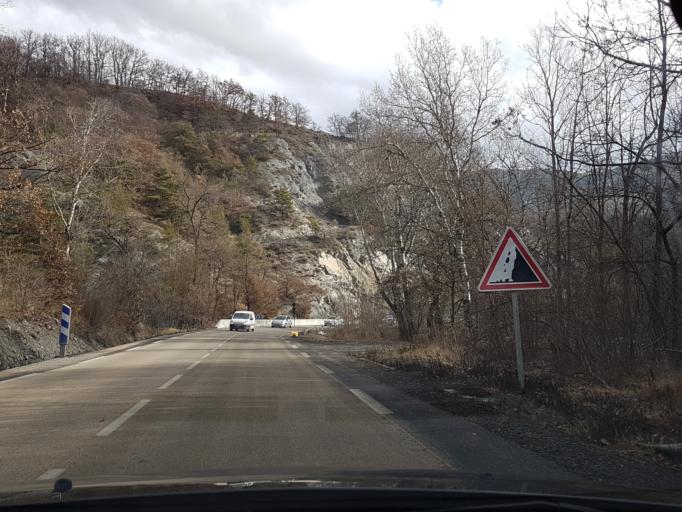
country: FR
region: Provence-Alpes-Cote d'Azur
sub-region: Departement des Hautes-Alpes
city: Tallard
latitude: 44.5110
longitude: 6.0772
